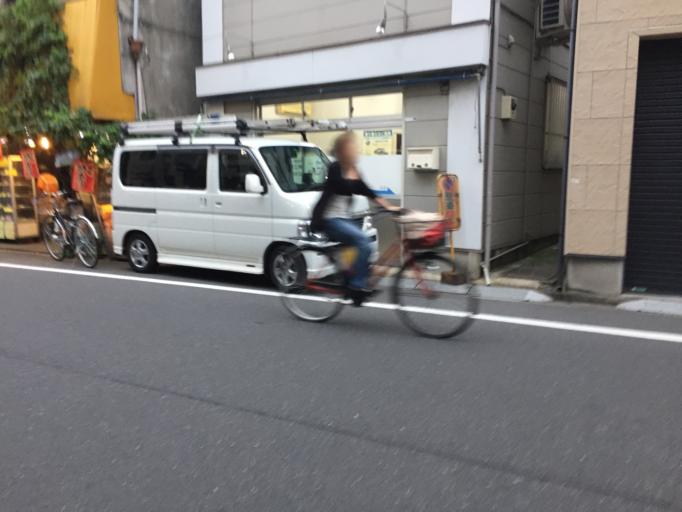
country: JP
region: Tokyo
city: Tokyo
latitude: 35.7138
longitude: 139.6690
